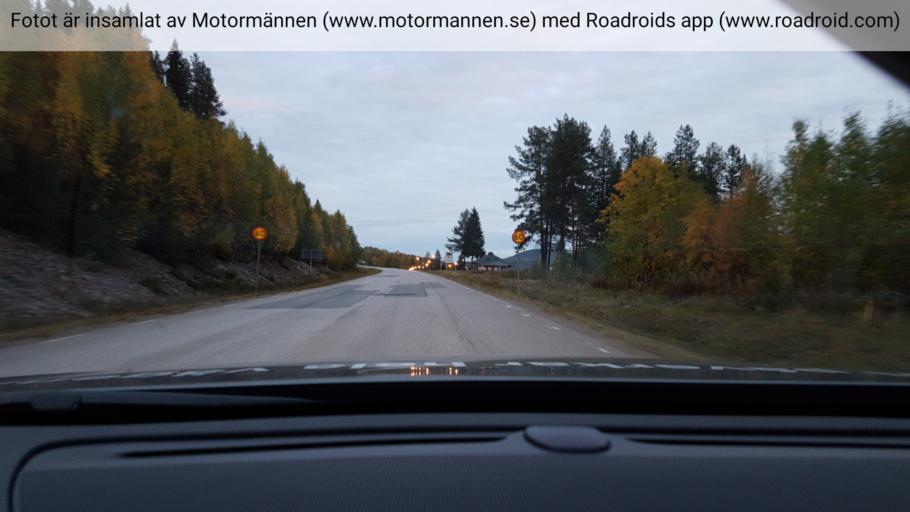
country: SE
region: Norrbotten
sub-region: Alvsbyns Kommun
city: AElvsbyn
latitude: 65.8596
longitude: 20.4180
